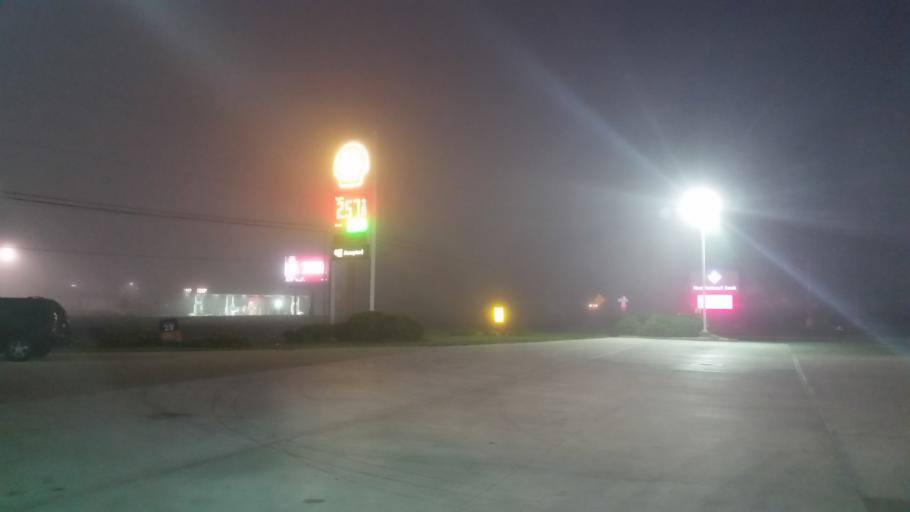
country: US
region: Ohio
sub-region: Hancock County
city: Findlay
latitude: 41.0586
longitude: -83.6722
